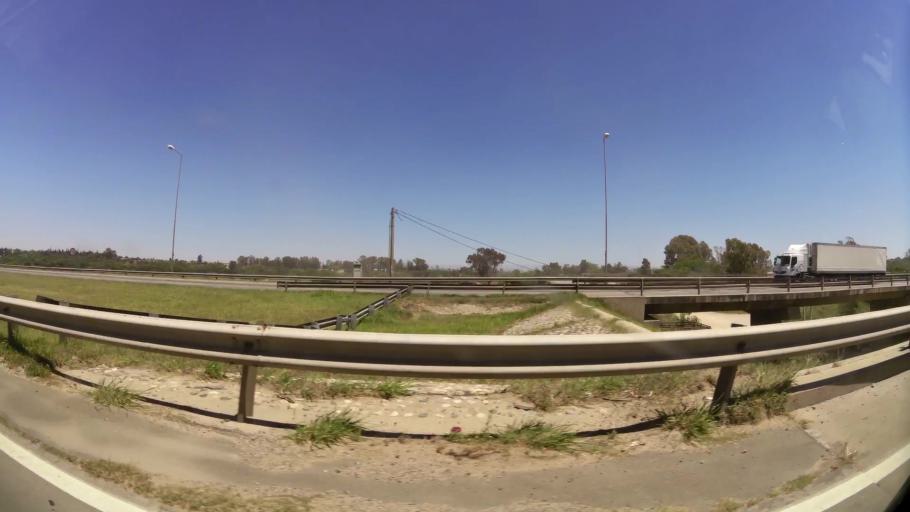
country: AR
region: Cordoba
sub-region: Departamento de Capital
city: Cordoba
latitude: -31.4029
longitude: -64.1261
